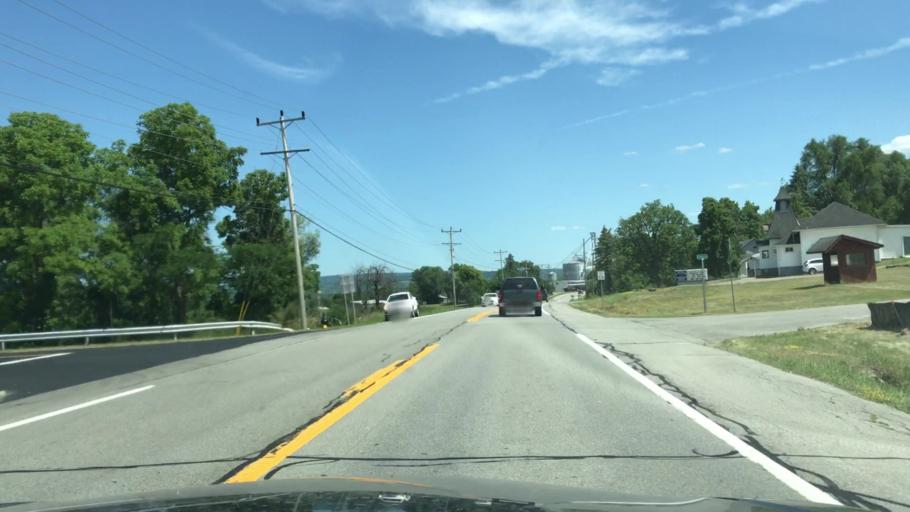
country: US
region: New York
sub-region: Livingston County
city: Mount Morris
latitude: 42.6806
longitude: -77.8229
